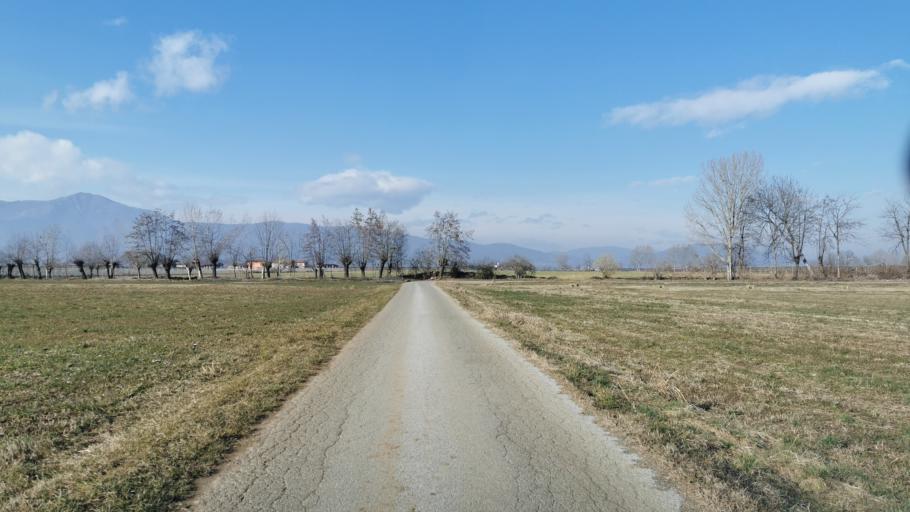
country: IT
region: Piedmont
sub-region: Provincia di Cuneo
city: Caraglio
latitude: 44.4444
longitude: 7.4463
